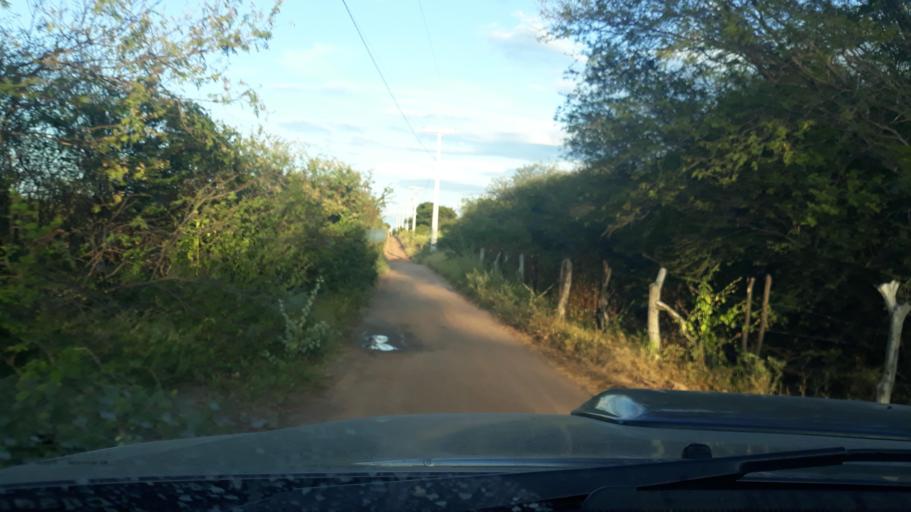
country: BR
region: Bahia
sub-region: Riacho De Santana
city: Riacho de Santana
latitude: -13.8611
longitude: -43.0309
